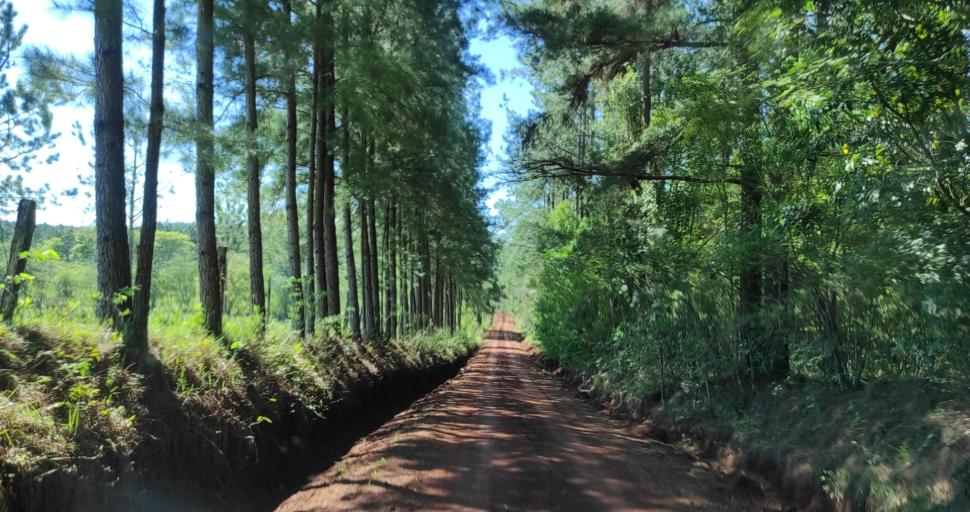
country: AR
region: Misiones
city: Ruiz de Montoya
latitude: -26.9502
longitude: -55.0032
